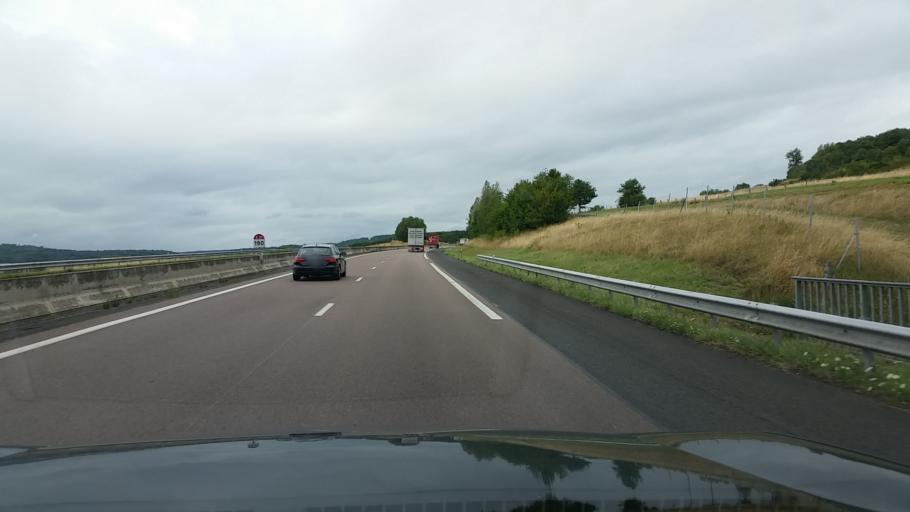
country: FR
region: Lorraine
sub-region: Departement des Vosges
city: Chatenois
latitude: 48.3350
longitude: 5.8546
